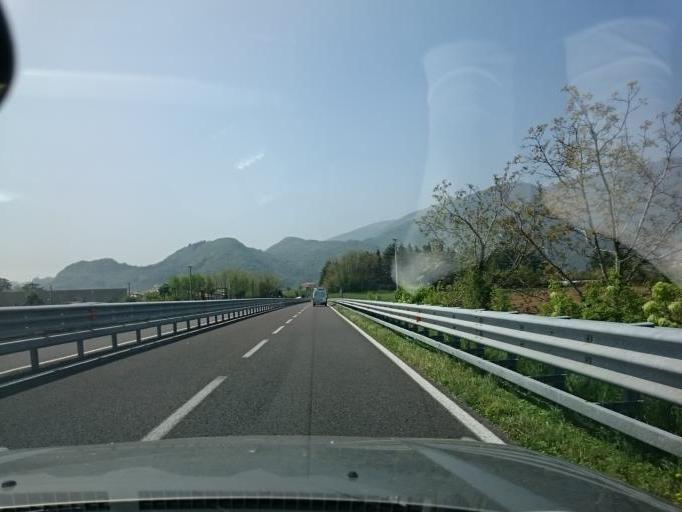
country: IT
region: Veneto
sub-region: Provincia di Vicenza
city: Pove del Grappa
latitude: 45.7890
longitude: 11.7404
